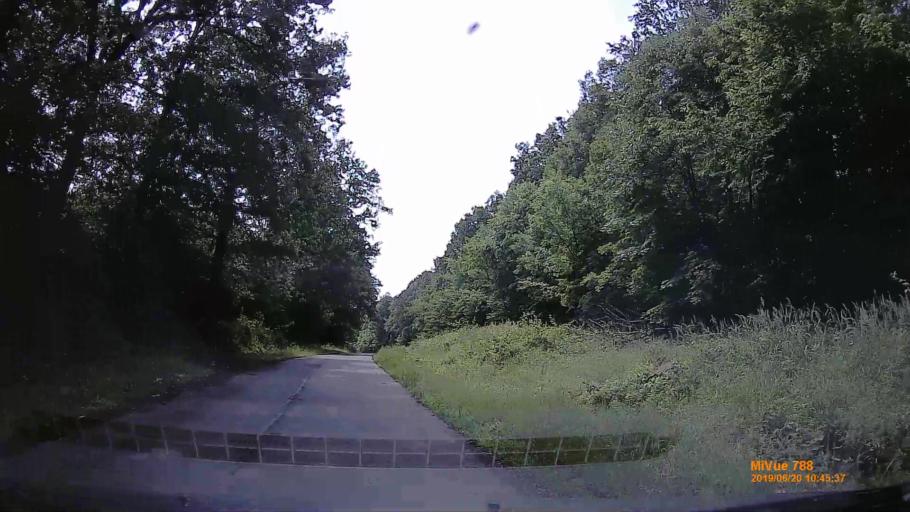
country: HU
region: Baranya
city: Hidas
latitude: 46.1821
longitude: 18.5723
